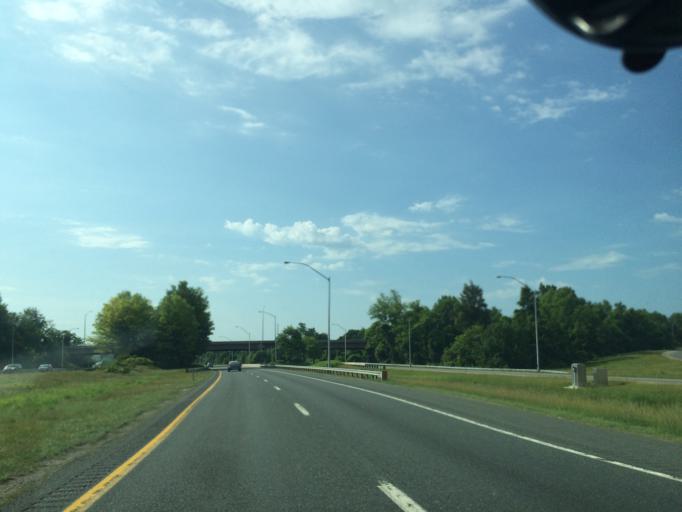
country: US
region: Maryland
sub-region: Baltimore County
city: Owings Mills
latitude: 39.4146
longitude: -76.7948
